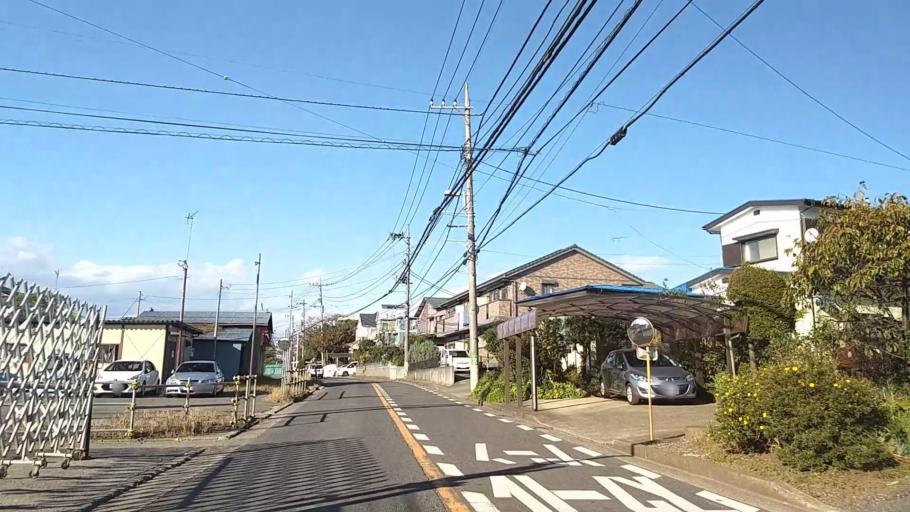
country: JP
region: Tokyo
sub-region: Machida-shi
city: Machida
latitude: 35.5364
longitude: 139.5448
